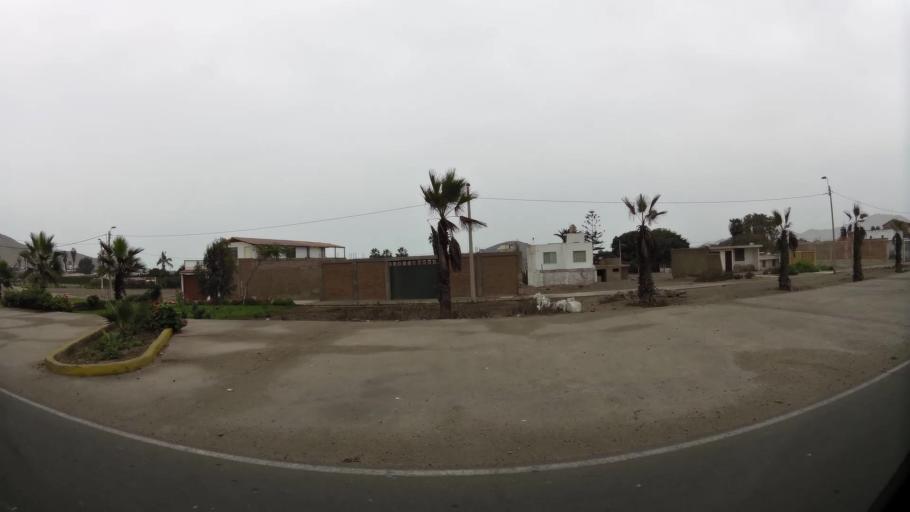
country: PE
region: Lima
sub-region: Lima
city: Santa Rosa
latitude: -11.8019
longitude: -77.1723
